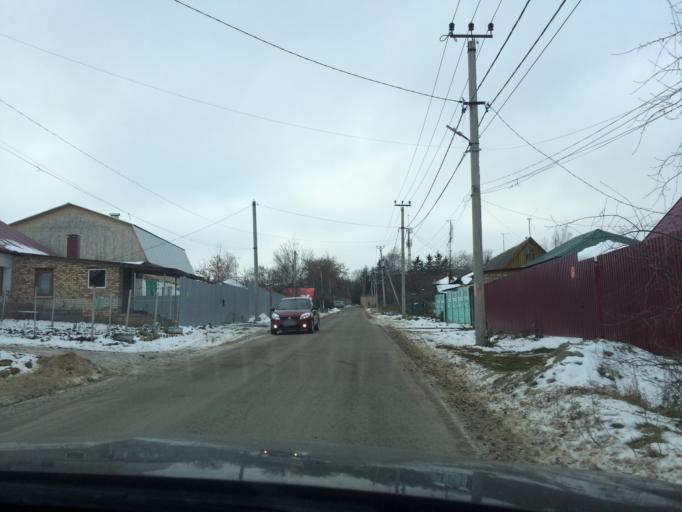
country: RU
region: Tula
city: Plavsk
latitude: 53.7071
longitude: 37.2977
